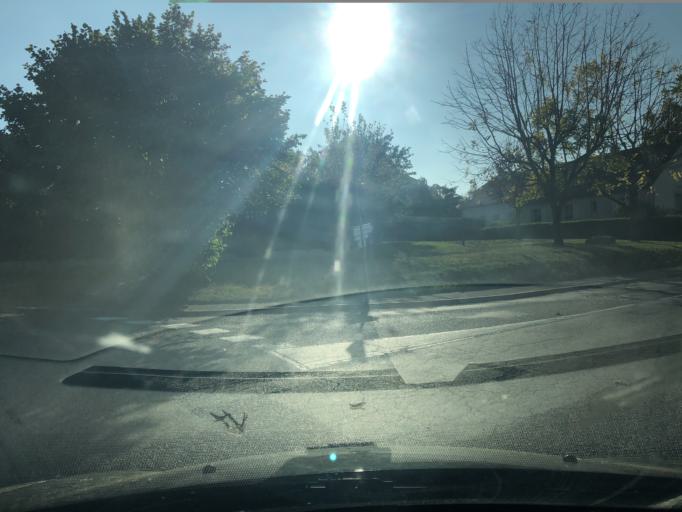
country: FR
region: Centre
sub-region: Departement d'Indre-et-Loire
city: Neuvy-le-Roi
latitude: 47.6061
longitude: 0.5967
